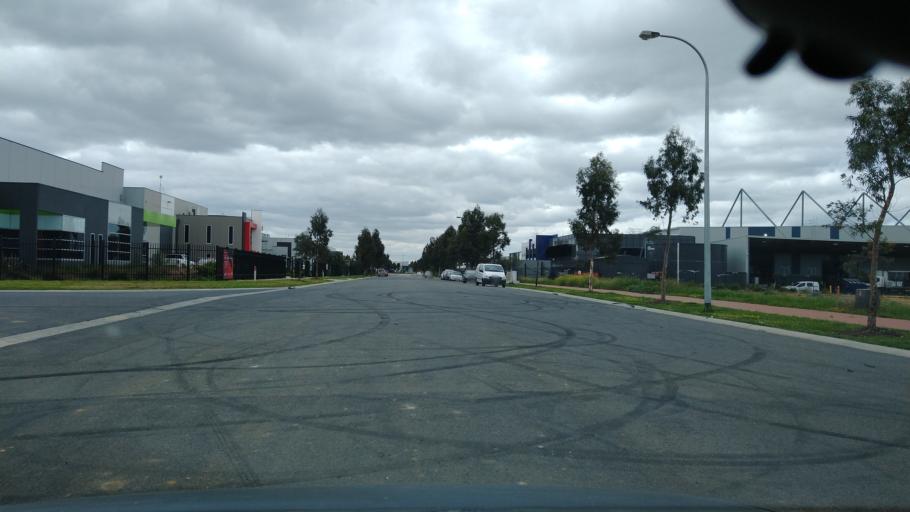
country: AU
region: Victoria
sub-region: Frankston
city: Sandhurst
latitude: -38.0579
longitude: 145.2149
